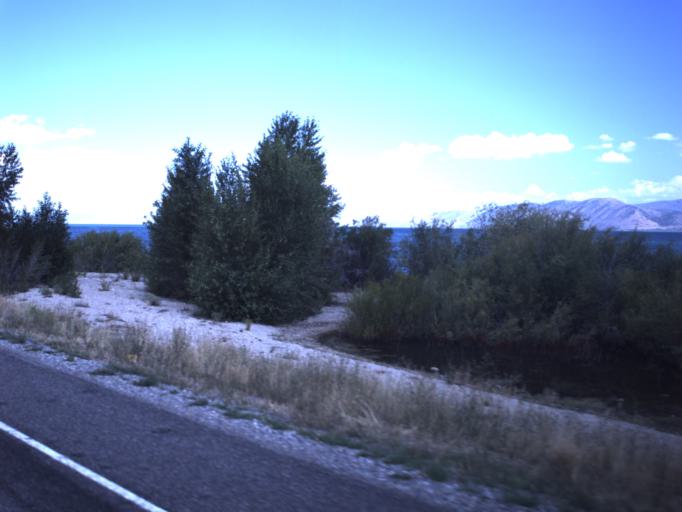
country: US
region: Utah
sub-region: Rich County
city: Randolph
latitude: 41.8586
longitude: -111.3649
